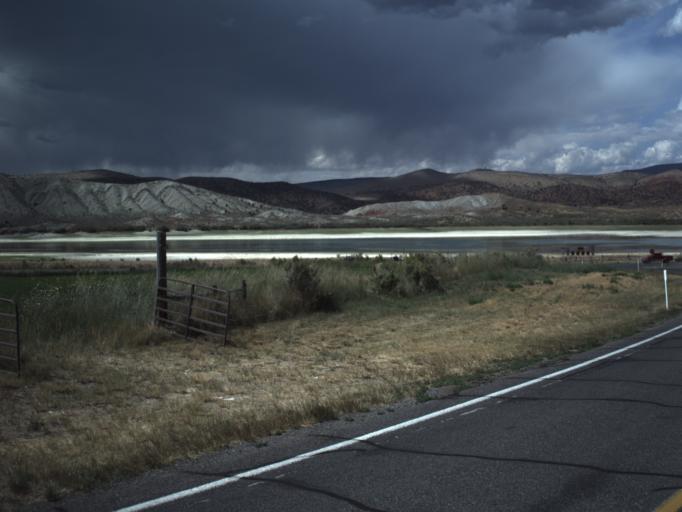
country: US
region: Utah
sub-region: Sanpete County
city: Gunnison
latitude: 39.1704
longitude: -111.7049
